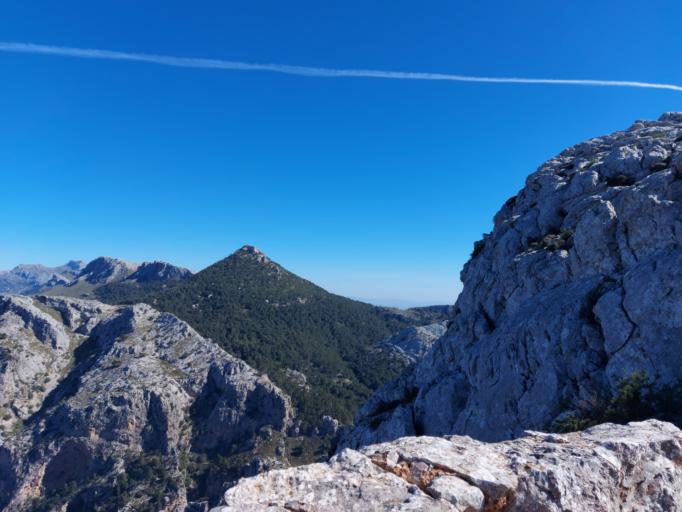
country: ES
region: Balearic Islands
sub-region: Illes Balears
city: Fornalutx
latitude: 39.7602
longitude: 2.7470
